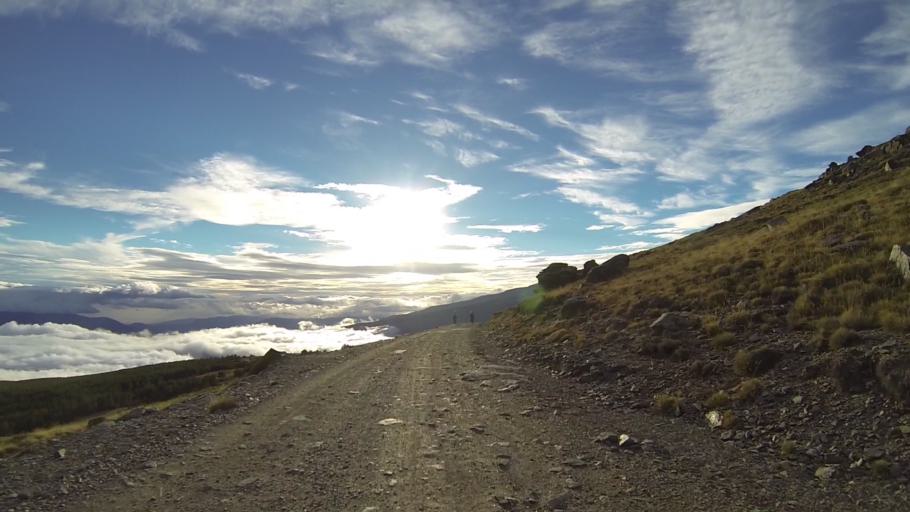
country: ES
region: Andalusia
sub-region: Provincia de Granada
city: Capileira
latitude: 36.9795
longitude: -3.3256
